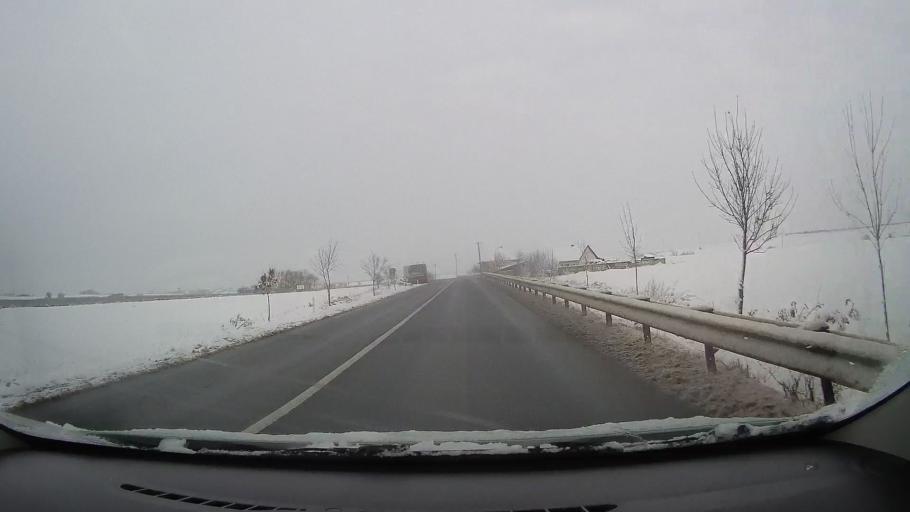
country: RO
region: Alba
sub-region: Municipiul Sebes
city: Lancram
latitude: 45.9812
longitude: 23.5183
